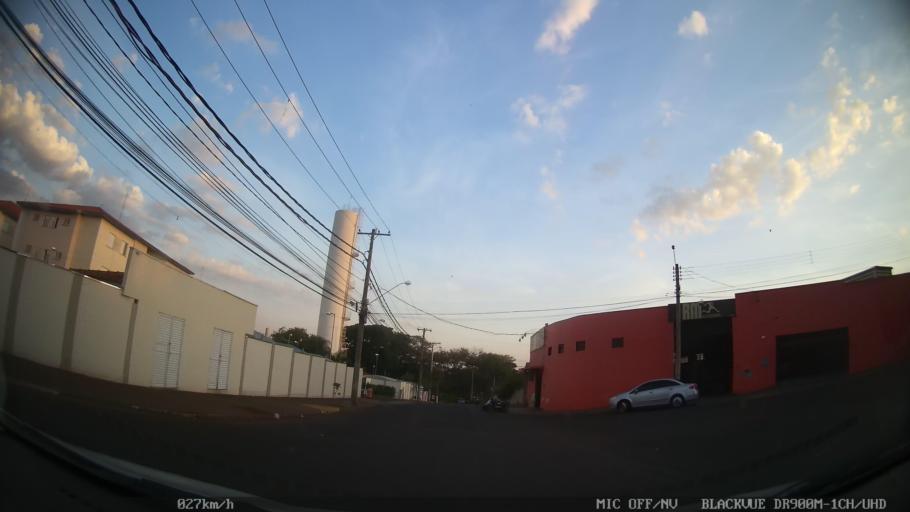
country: BR
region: Sao Paulo
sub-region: Ribeirao Preto
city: Ribeirao Preto
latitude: -21.1208
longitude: -47.8179
